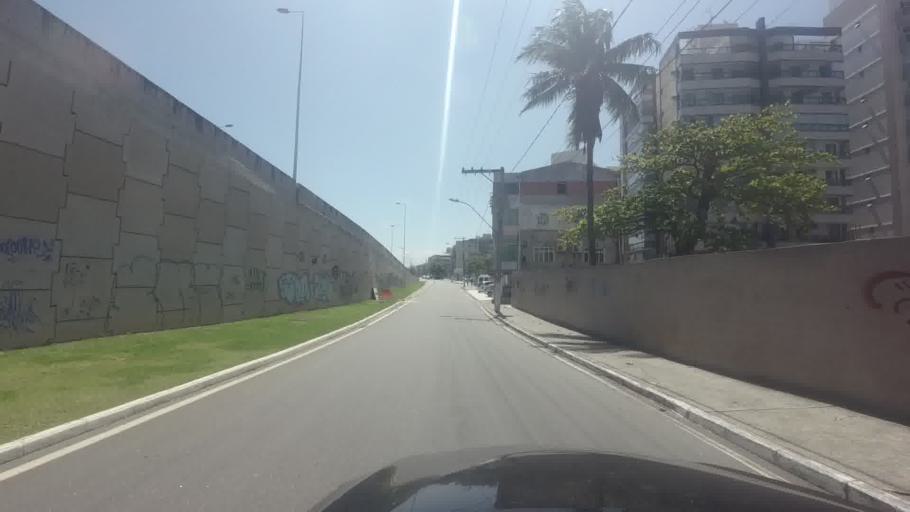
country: BR
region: Espirito Santo
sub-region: Vila Velha
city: Vila Velha
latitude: -20.2641
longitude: -40.2611
